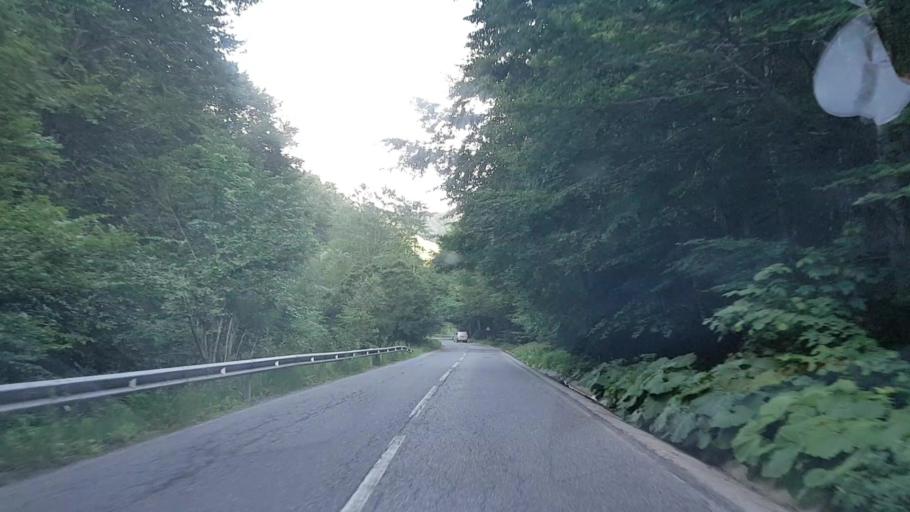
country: RO
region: Harghita
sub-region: Comuna Praid
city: Ocna de Sus
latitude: 46.5969
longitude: 25.2399
